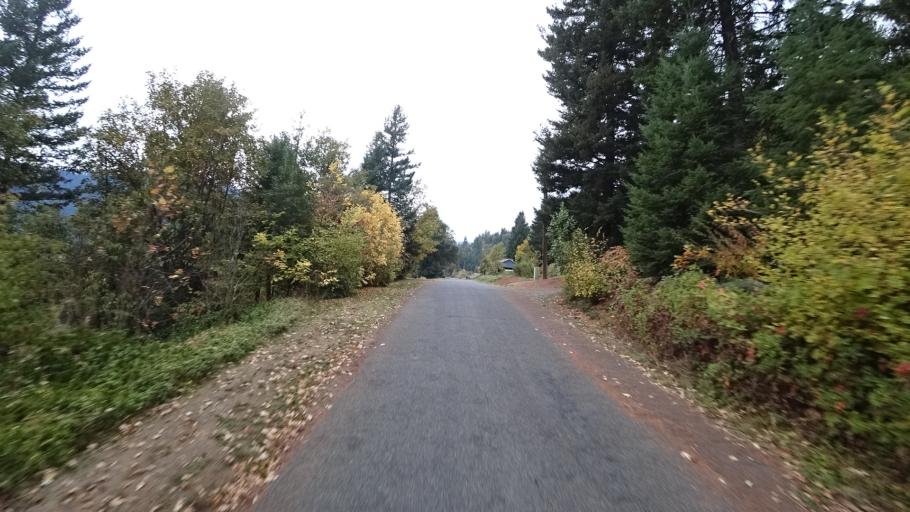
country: US
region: California
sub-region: Siskiyou County
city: Happy Camp
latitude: 41.8061
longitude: -123.3695
